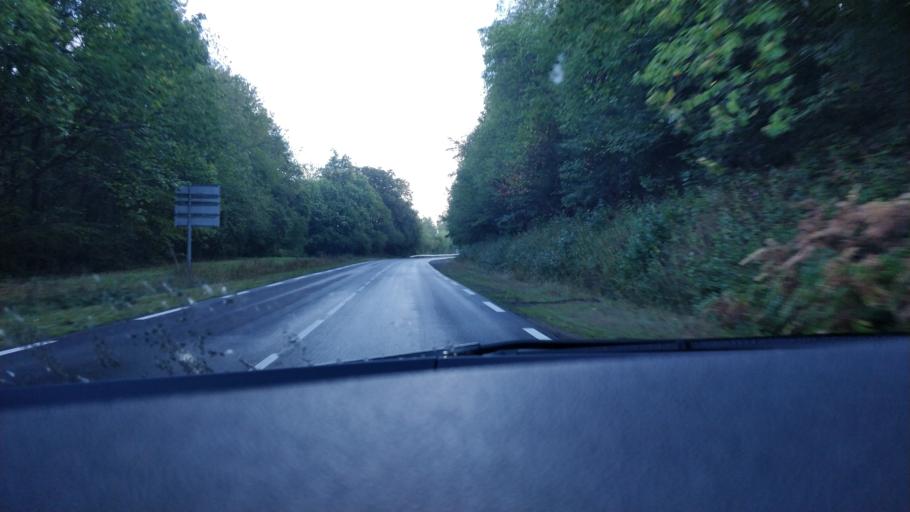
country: FR
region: Limousin
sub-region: Departement de la Haute-Vienne
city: Sauviat-sur-Vige
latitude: 45.9015
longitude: 1.5886
